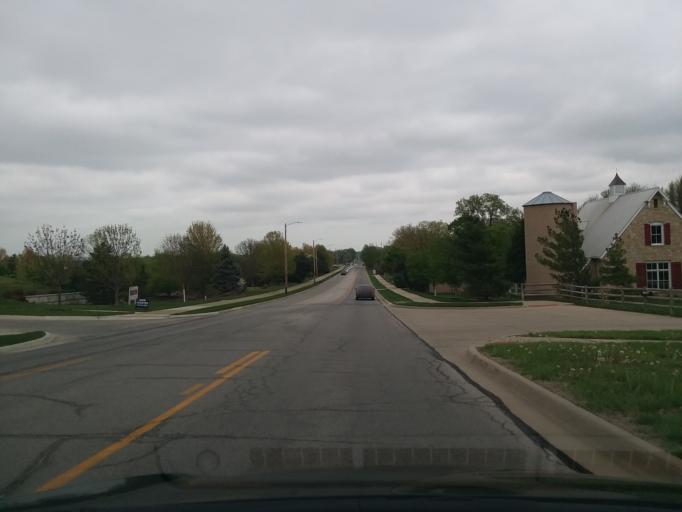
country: US
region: Kansas
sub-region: Douglas County
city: Lawrence
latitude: 38.9861
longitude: -95.2853
